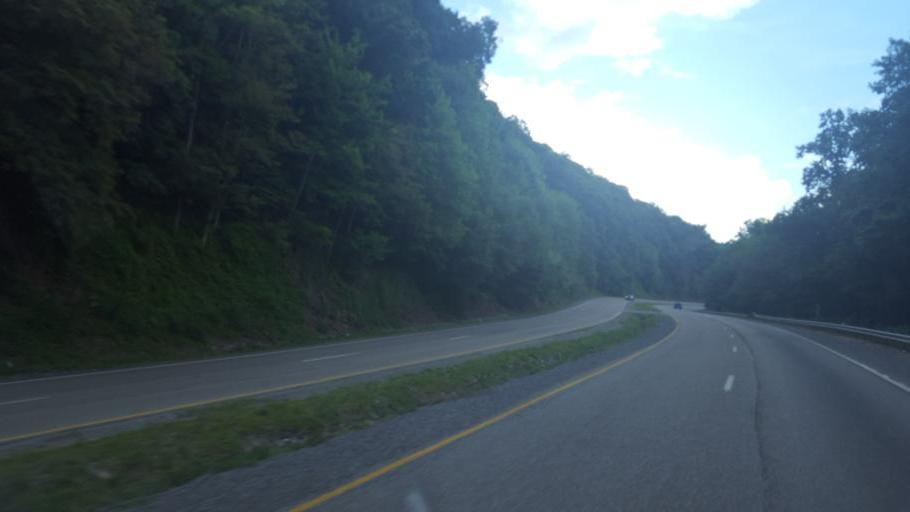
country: US
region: Virginia
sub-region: Wise County
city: Wise
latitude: 37.0233
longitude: -82.5909
